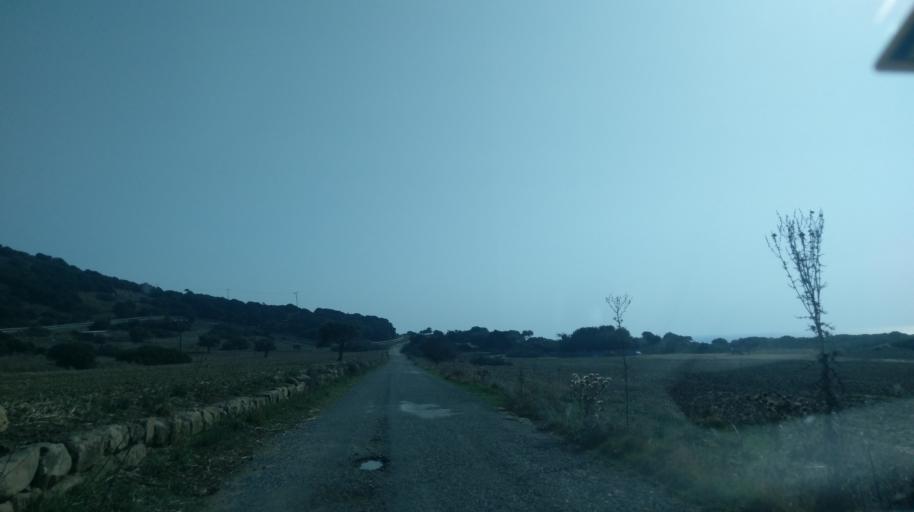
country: CY
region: Ammochostos
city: Rizokarpaso
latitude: 35.6482
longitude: 34.5524
